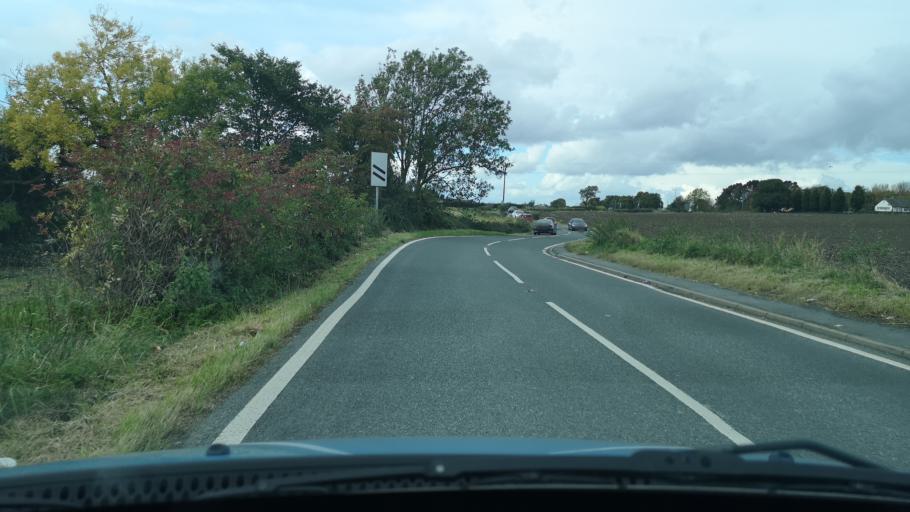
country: GB
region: England
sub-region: City and Borough of Wakefield
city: Featherstone
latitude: 53.6652
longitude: -1.3504
